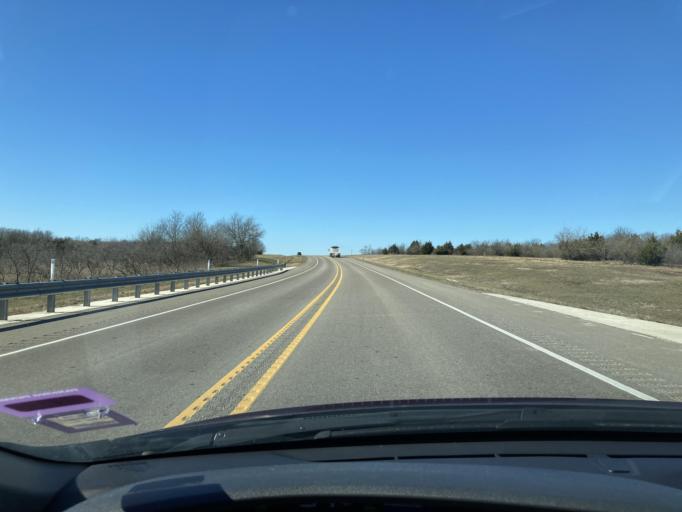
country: US
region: Texas
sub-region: Navarro County
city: Corsicana
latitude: 32.0479
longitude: -96.4760
